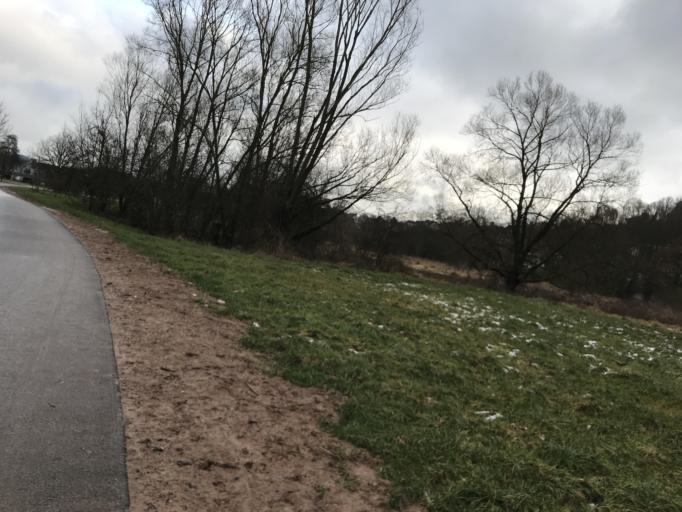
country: DE
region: Hesse
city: Frankenberg
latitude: 51.0606
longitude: 8.7932
